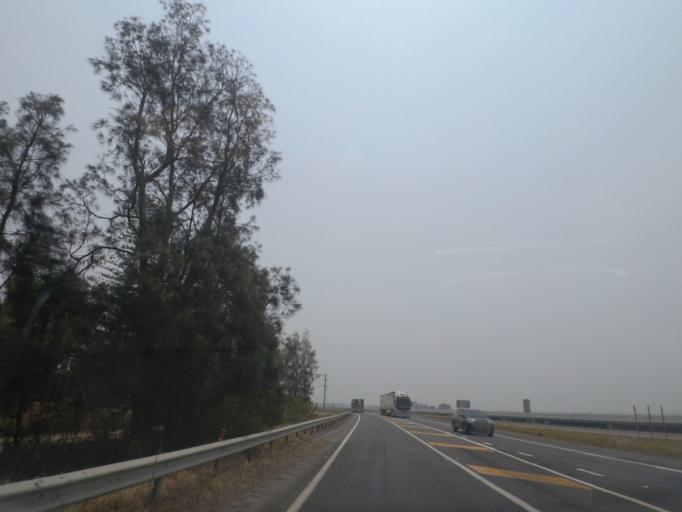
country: AU
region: New South Wales
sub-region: Clarence Valley
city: Maclean
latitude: -29.4179
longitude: 153.2409
